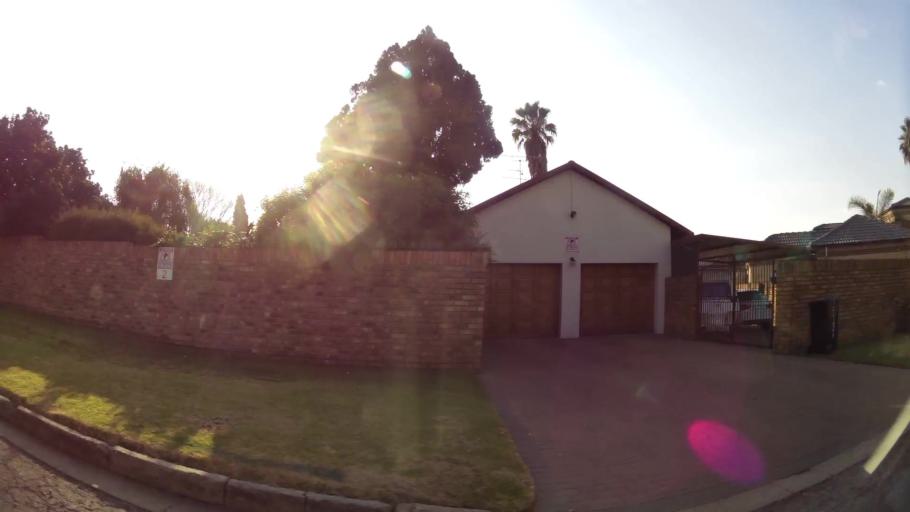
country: ZA
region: Gauteng
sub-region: City of Johannesburg Metropolitan Municipality
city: Modderfontein
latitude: -26.0763
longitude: 28.2095
